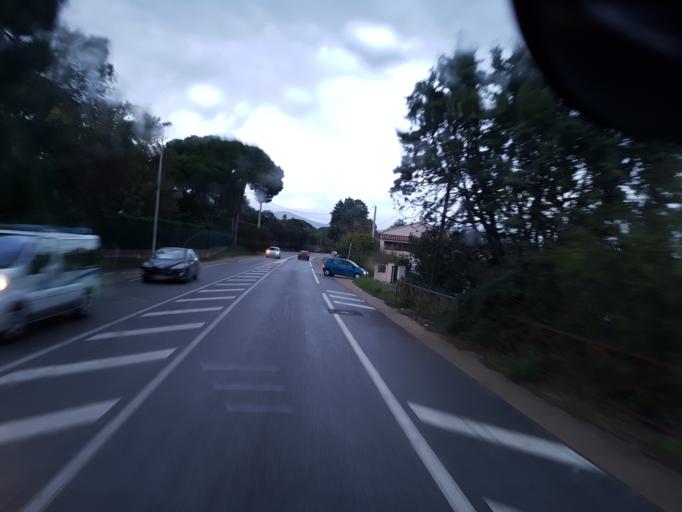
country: FR
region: Provence-Alpes-Cote d'Azur
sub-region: Departement du Var
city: Gassin
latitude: 43.2545
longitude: 6.5747
